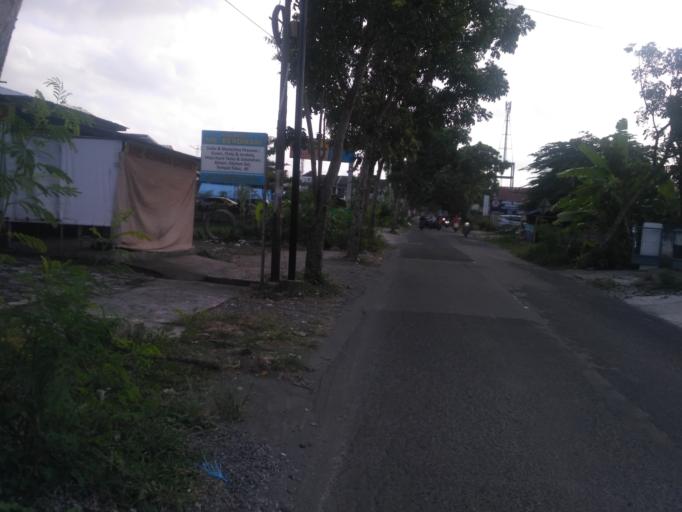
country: ID
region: Daerah Istimewa Yogyakarta
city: Yogyakarta
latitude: -7.7670
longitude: 110.3440
